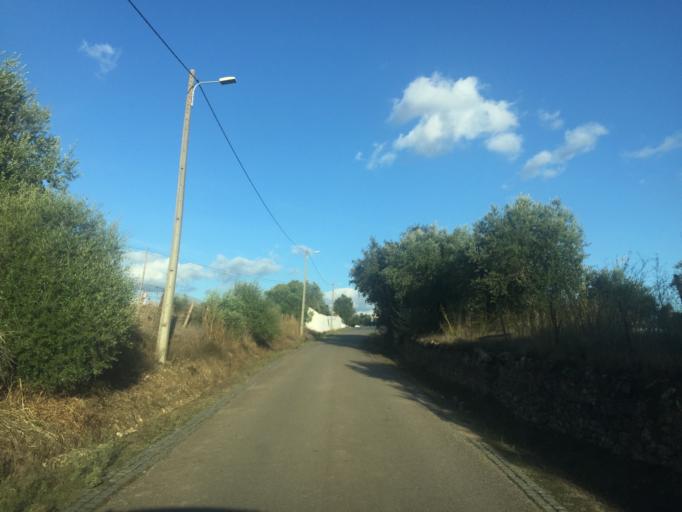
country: PT
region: Portalegre
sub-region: Alter do Chao
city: Alter do Chao
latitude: 39.1968
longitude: -7.6687
